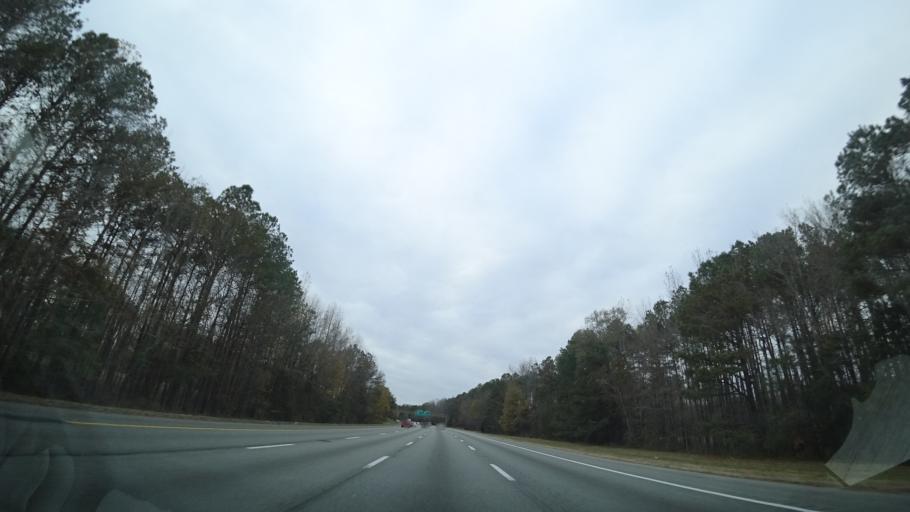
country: US
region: Virginia
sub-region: Henrico County
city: Highland Springs
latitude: 37.5759
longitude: -77.3136
